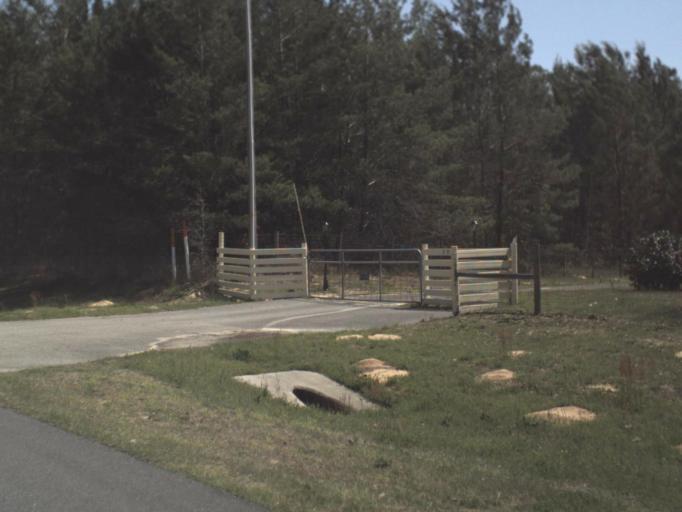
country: US
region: Florida
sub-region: Bay County
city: Youngstown
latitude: 30.4368
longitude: -85.3406
